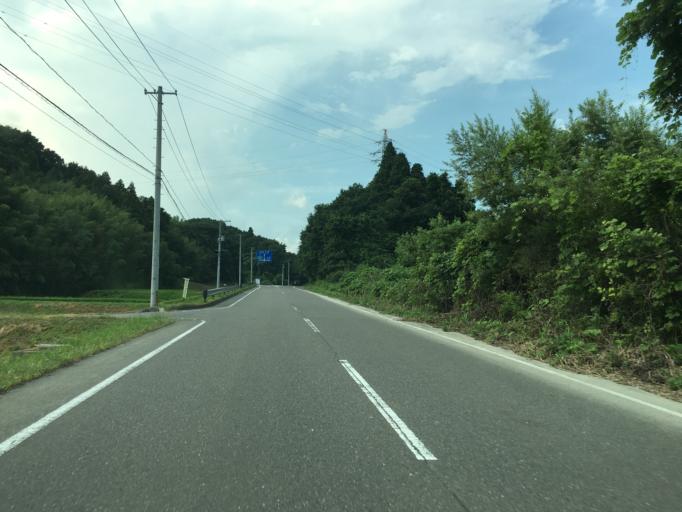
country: JP
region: Fukushima
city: Motomiya
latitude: 37.4885
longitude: 140.4124
